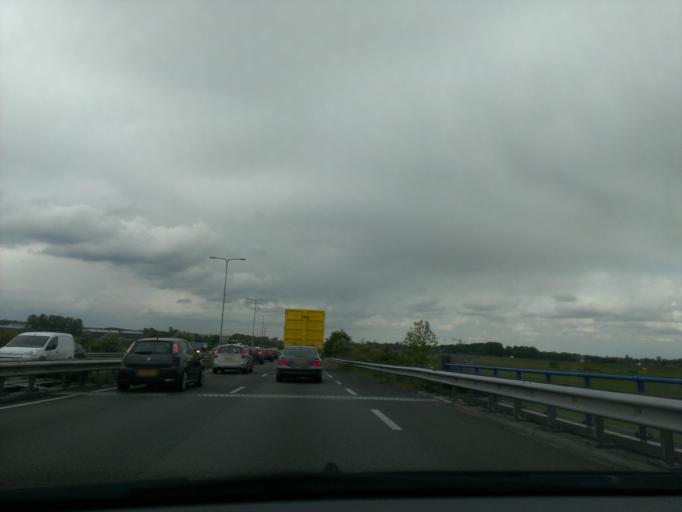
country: NL
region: Gelderland
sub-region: Gemeente Westervoort
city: Westervoort
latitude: 51.9598
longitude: 5.9421
